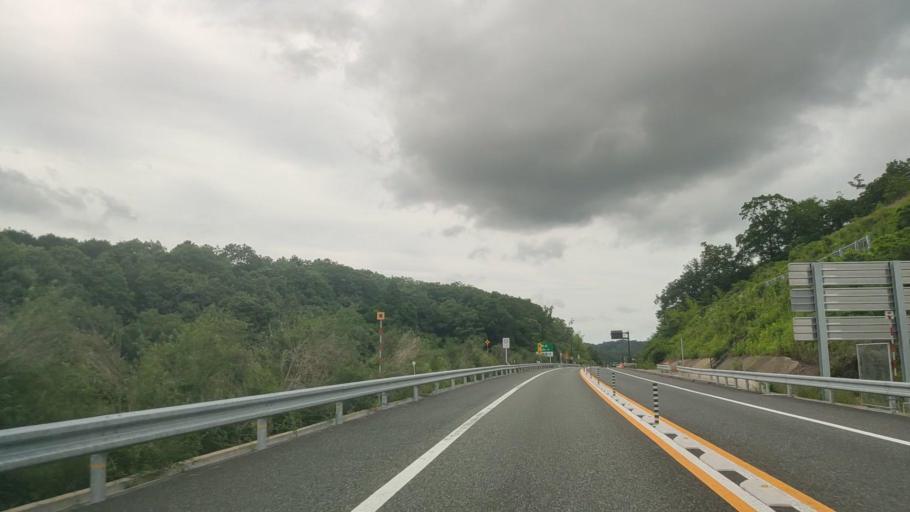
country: JP
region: Kyoto
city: Miyazu
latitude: 35.5670
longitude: 135.1206
